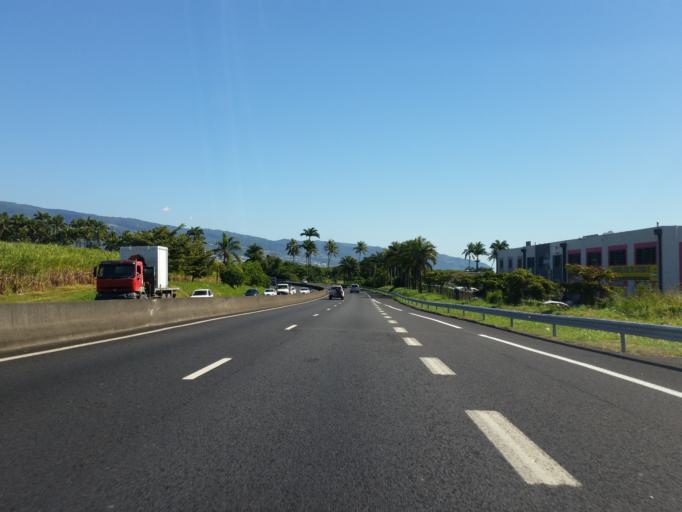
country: RE
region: Reunion
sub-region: Reunion
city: Sainte-Marie
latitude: -20.8979
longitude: 55.5654
